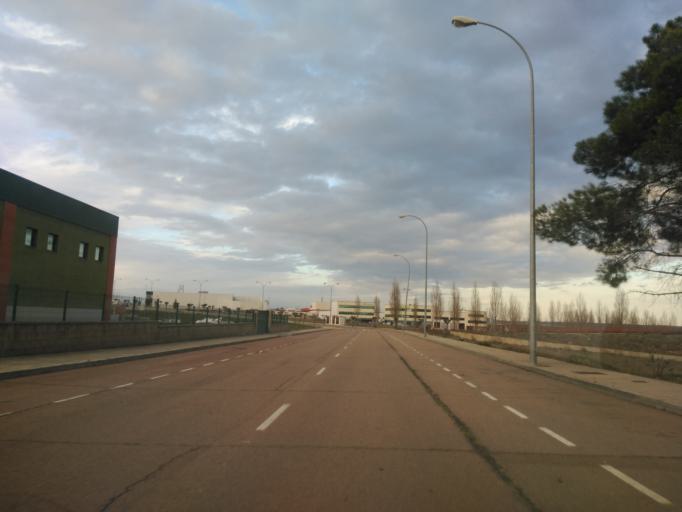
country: ES
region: Castille and Leon
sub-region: Provincia de Salamanca
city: Carbajosa de la Sagrada
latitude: 40.9371
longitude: -5.6536
